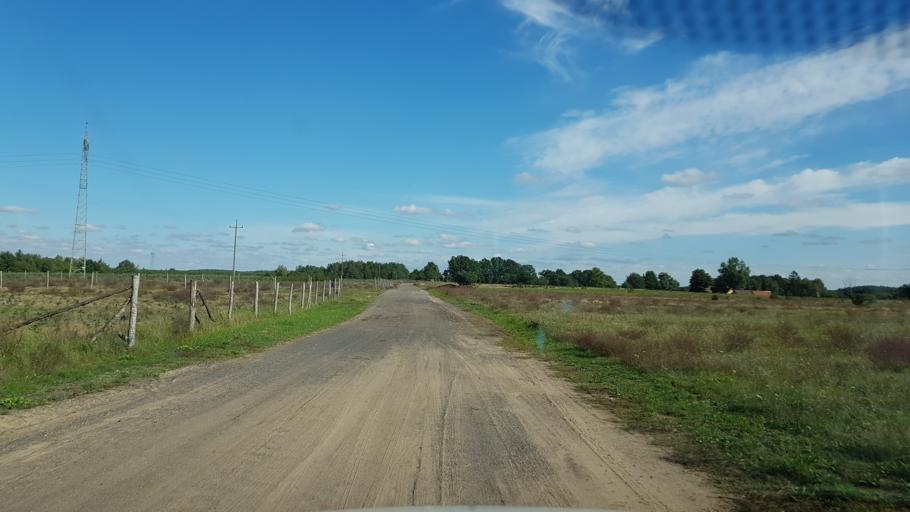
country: PL
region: Lubusz
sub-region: Powiat gorzowski
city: Lubiszyn
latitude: 52.8526
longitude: 14.9564
